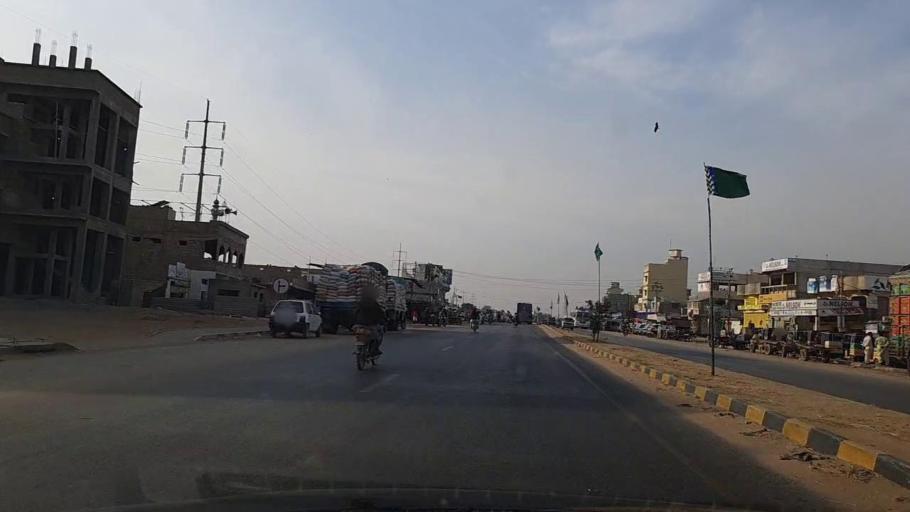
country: PK
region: Sindh
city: Gharo
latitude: 24.7903
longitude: 67.5260
